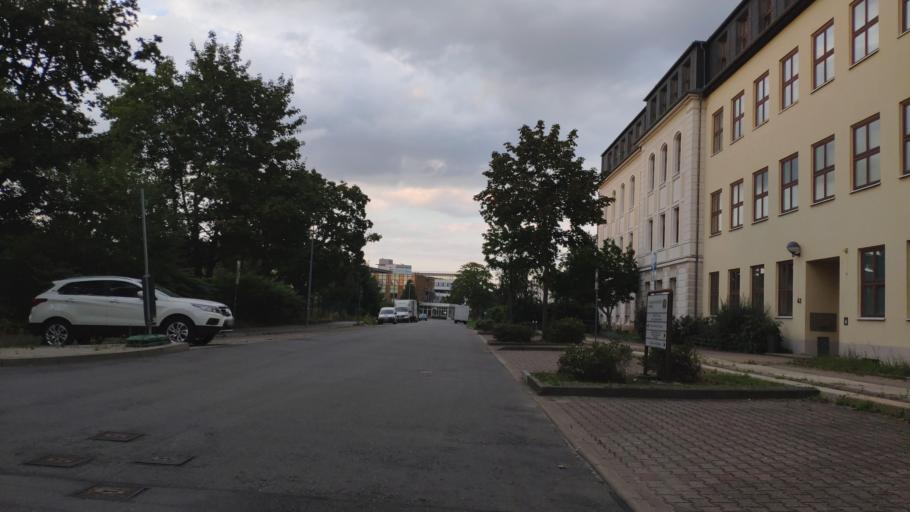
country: DE
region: Saxony
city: Chemnitz
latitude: 50.8177
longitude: 12.9165
